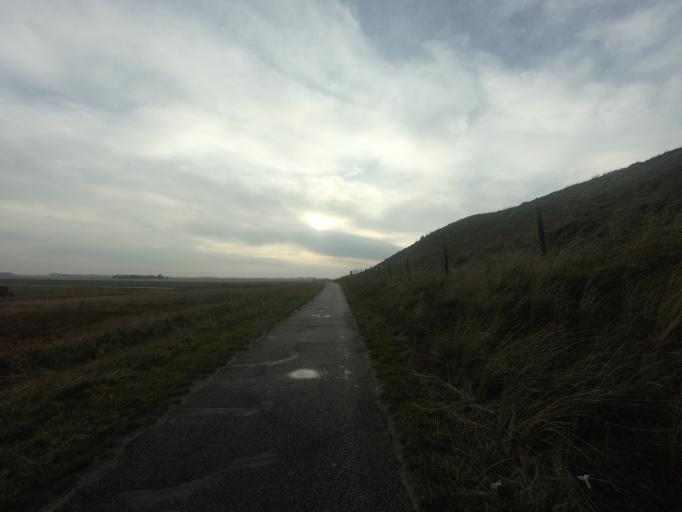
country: NL
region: North Holland
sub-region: Gemeente Texel
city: Den Burg
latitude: 53.1468
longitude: 4.8349
